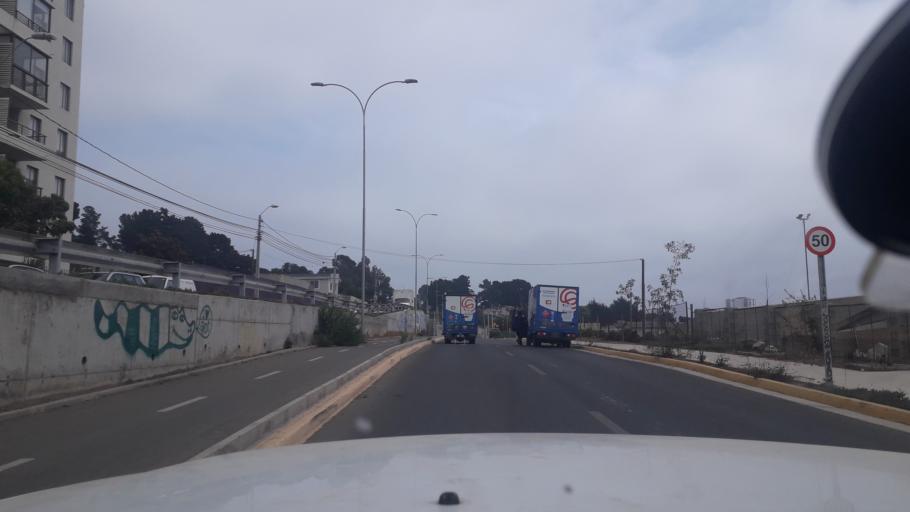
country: CL
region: Valparaiso
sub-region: Provincia de Valparaiso
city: Vina del Mar
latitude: -32.9373
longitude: -71.5341
